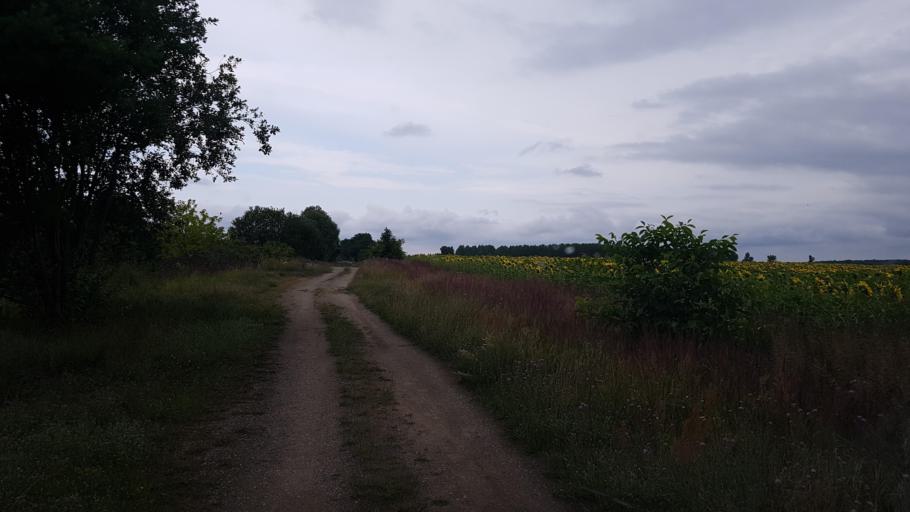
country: DE
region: Brandenburg
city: Spremberg
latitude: 51.5915
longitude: 14.3198
